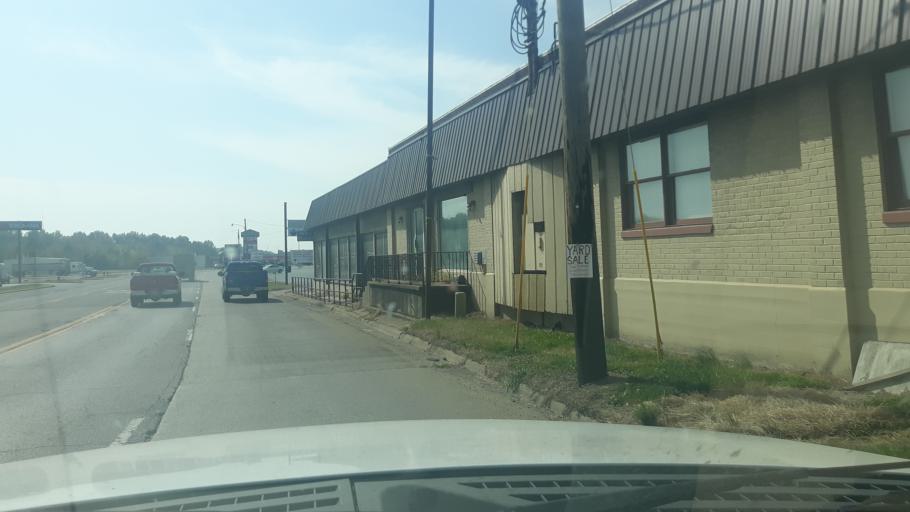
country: US
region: Illinois
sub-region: Saline County
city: Harrisburg
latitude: 37.7369
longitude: -88.5333
